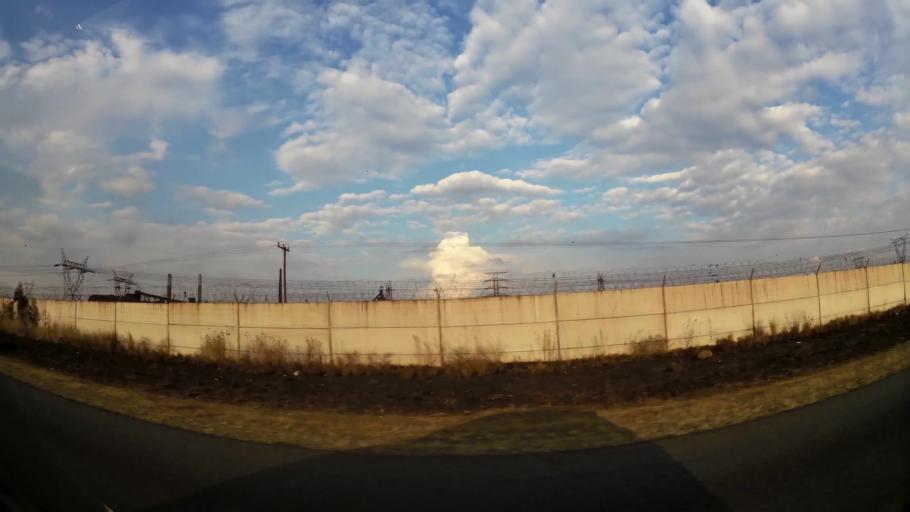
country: ZA
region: Gauteng
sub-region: Sedibeng District Municipality
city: Vanderbijlpark
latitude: -26.6580
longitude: 27.8009
